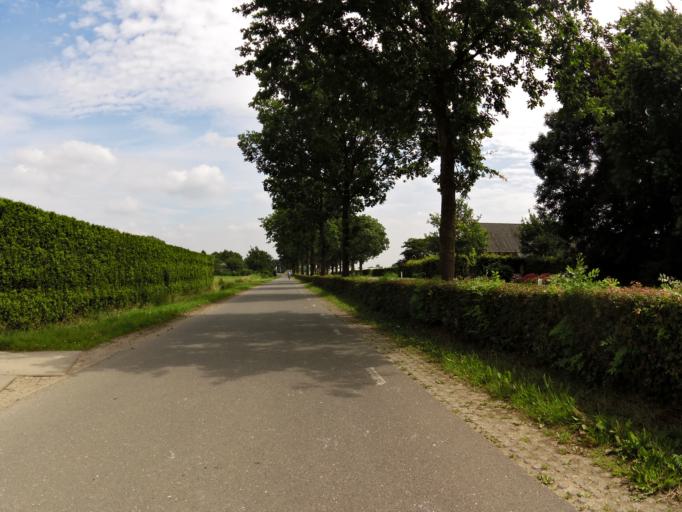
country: NL
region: South Holland
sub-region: Gemeente Leerdam
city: Leerdam
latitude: 51.8818
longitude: 5.1472
